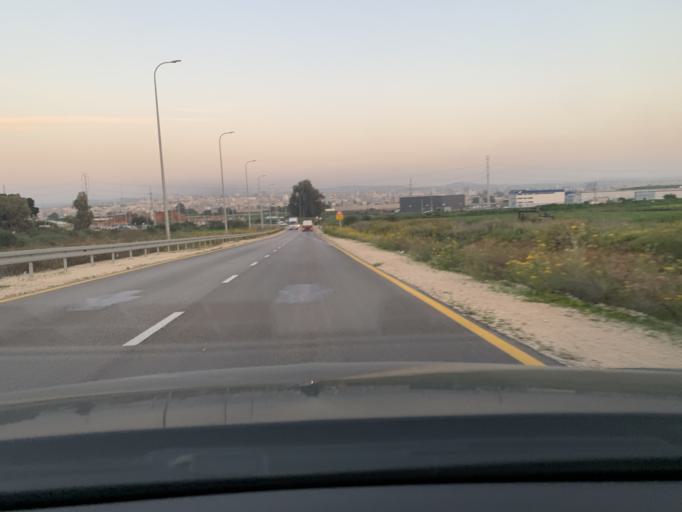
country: PS
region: West Bank
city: Qalqilyah
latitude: 32.1932
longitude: 34.9489
